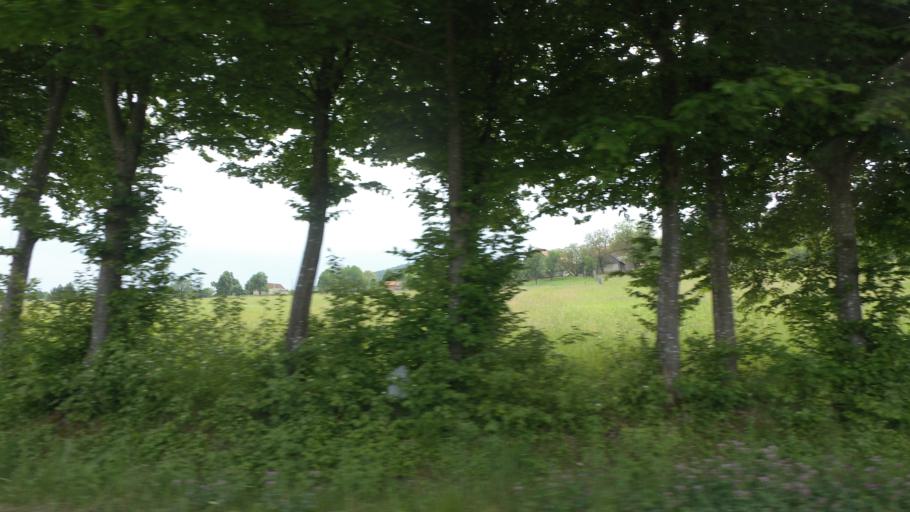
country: HR
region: Karlovacka
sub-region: Grad Karlovac
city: Karlovac
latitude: 45.4157
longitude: 15.5929
